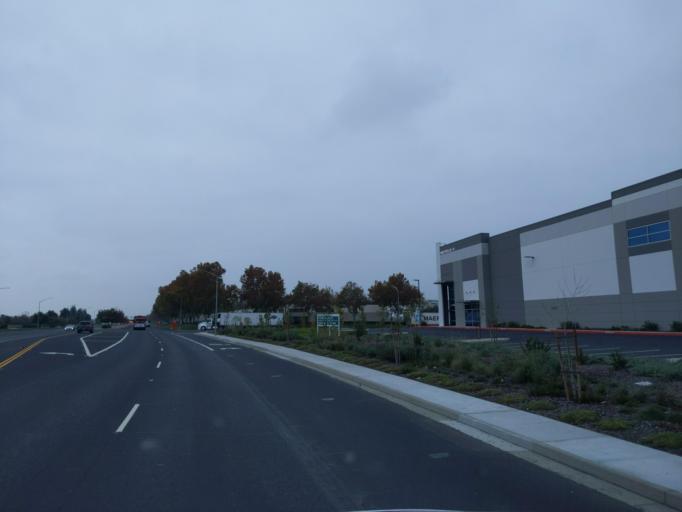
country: US
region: California
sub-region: San Joaquin County
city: Kennedy
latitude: 37.9074
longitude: -121.2371
